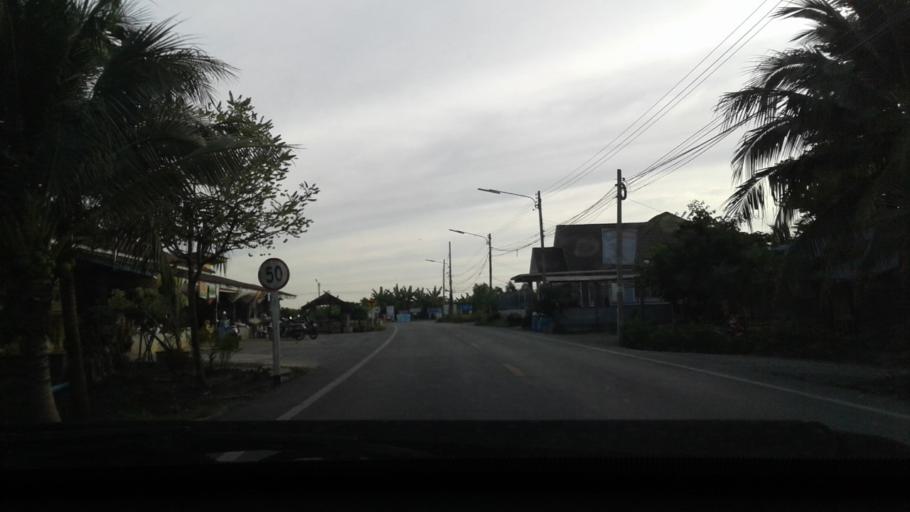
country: TH
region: Nonthaburi
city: Sai Noi
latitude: 13.9051
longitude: 100.2574
